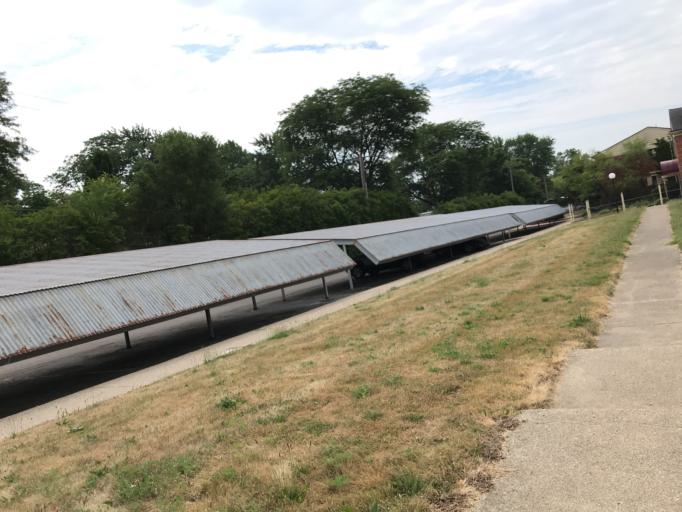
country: US
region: Michigan
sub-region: Washtenaw County
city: Ann Arbor
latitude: 42.2437
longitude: -83.7134
